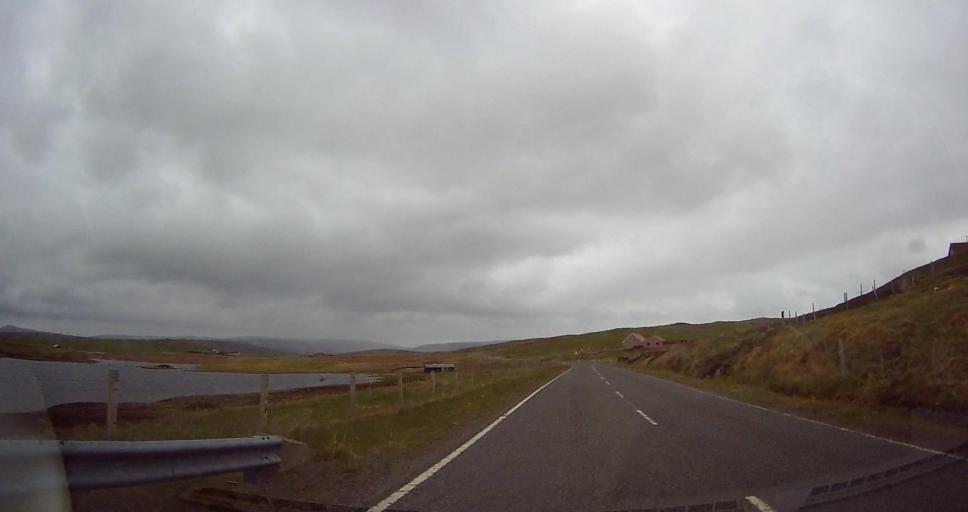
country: GB
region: Scotland
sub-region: Shetland Islands
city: Lerwick
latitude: 60.2564
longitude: -1.4679
